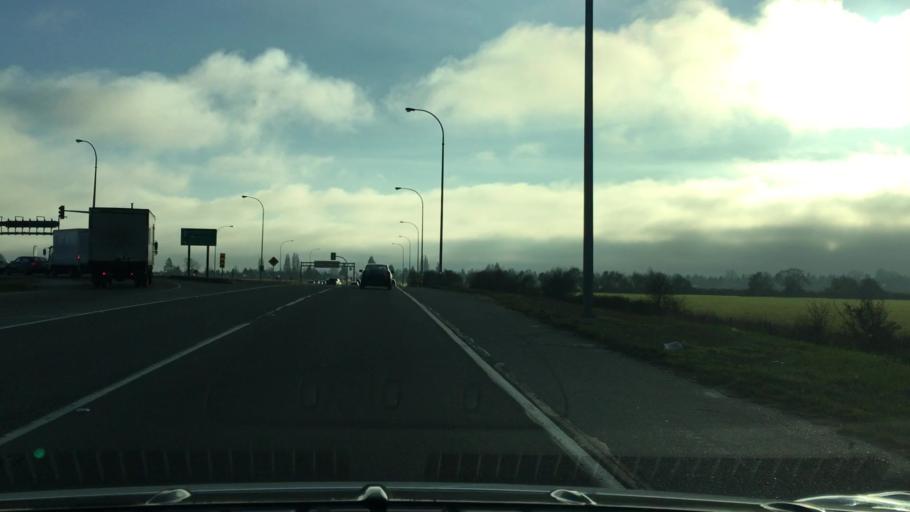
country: CA
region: British Columbia
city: Ladner
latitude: 49.1074
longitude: -123.0575
